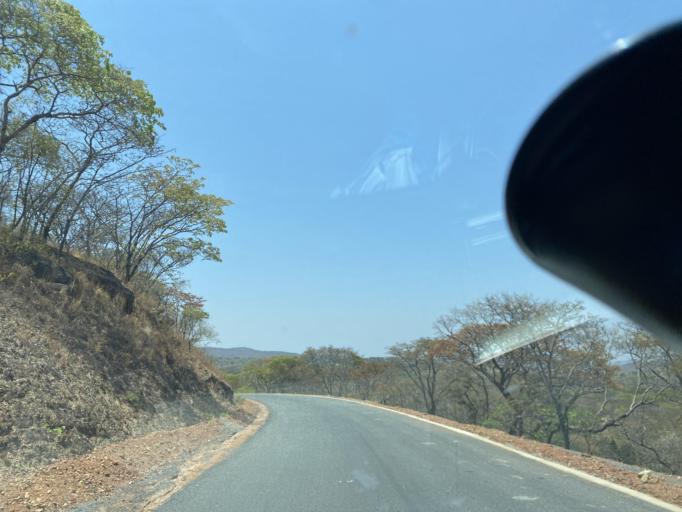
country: ZM
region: Lusaka
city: Kafue
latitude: -15.8589
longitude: 28.4226
